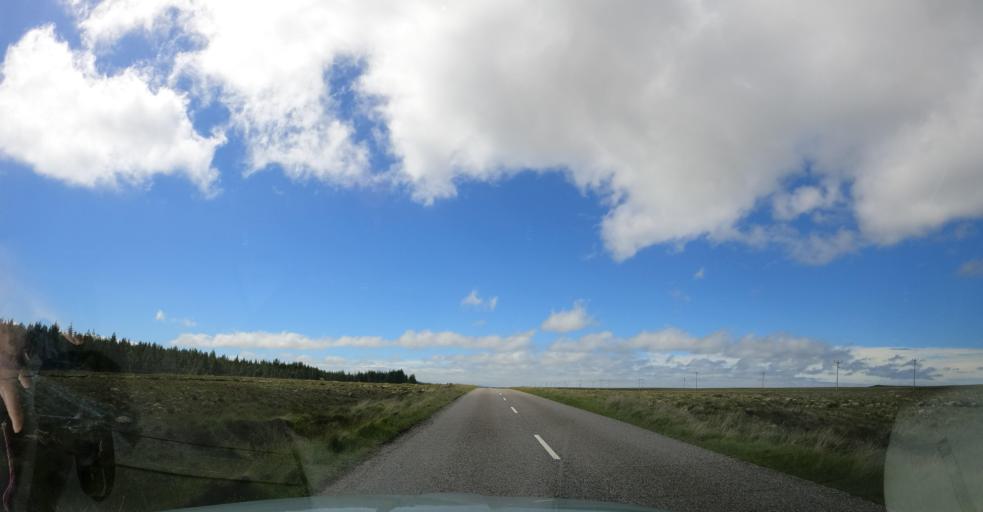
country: GB
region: Scotland
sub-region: Eilean Siar
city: Isle of Lewis
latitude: 58.1791
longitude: -6.6445
